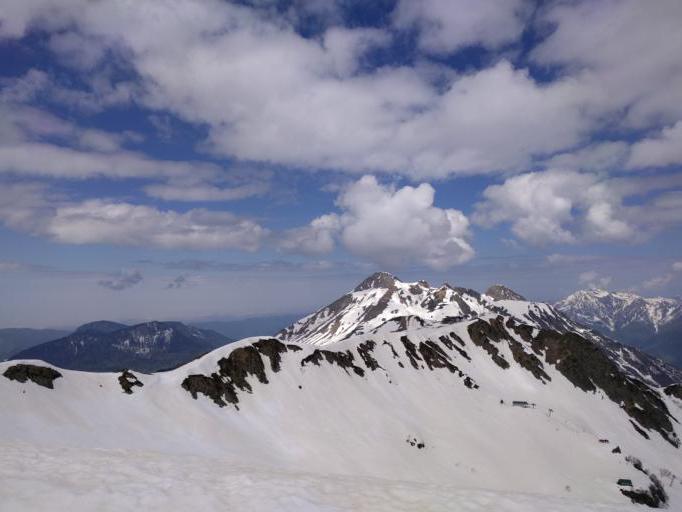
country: RU
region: Krasnodarskiy
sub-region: Sochi City
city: Krasnaya Polyana
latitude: 43.6255
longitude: 40.3102
